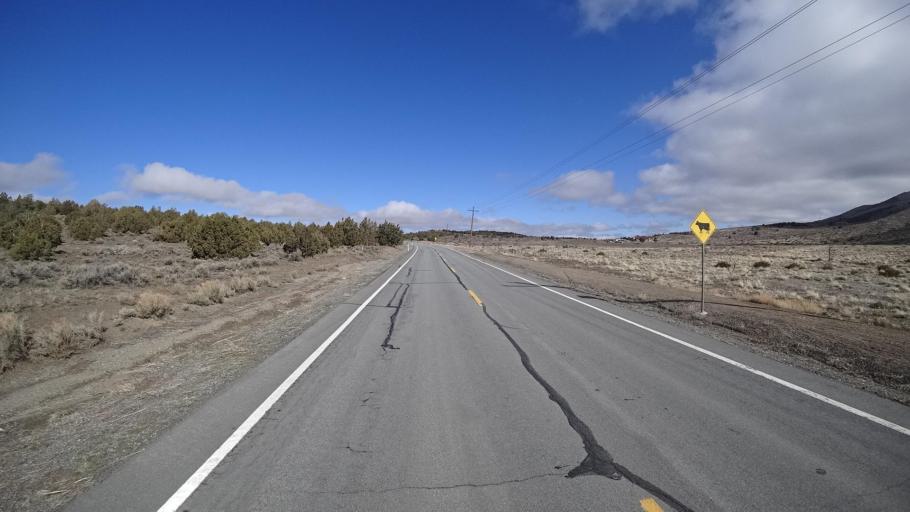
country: US
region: Nevada
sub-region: Washoe County
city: Cold Springs
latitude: 39.7678
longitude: -119.8866
